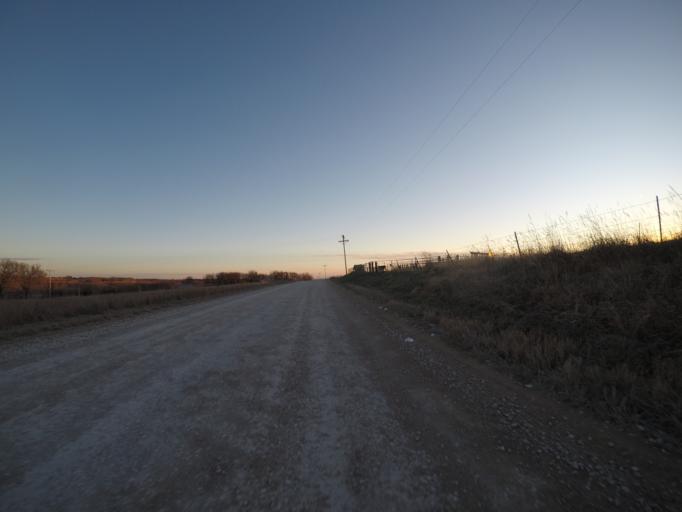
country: US
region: Kansas
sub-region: Riley County
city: Manhattan
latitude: 39.2628
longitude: -96.4827
